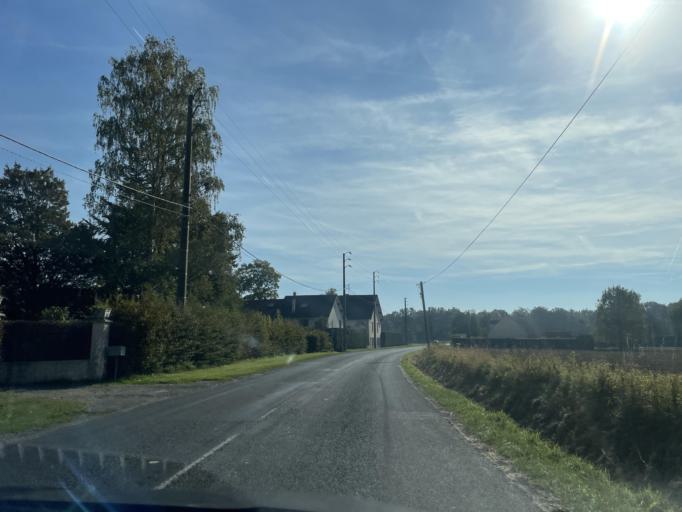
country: FR
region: Ile-de-France
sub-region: Departement de Seine-et-Marne
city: Sammeron
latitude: 48.8970
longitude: 3.0598
